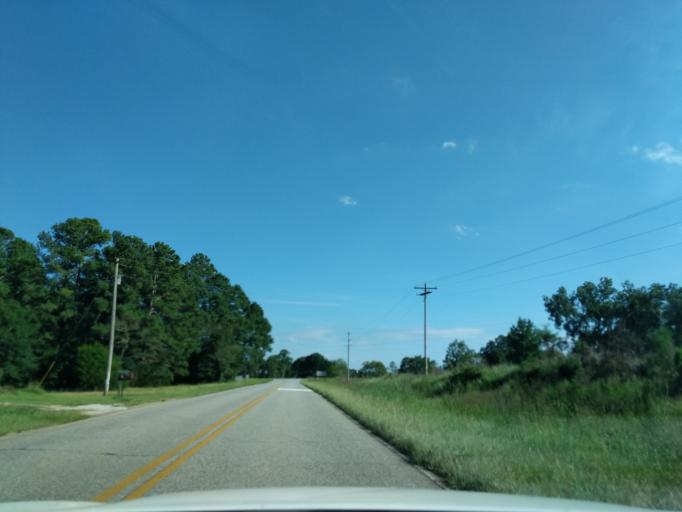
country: US
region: Georgia
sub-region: Oglethorpe County
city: Lexington
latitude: 33.9409
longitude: -83.0598
